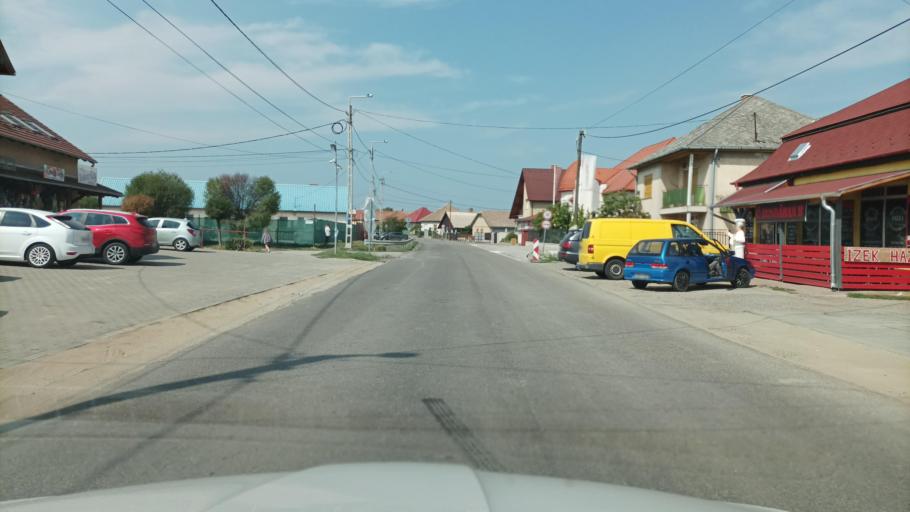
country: HU
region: Pest
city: Tura
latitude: 47.6106
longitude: 19.5892
